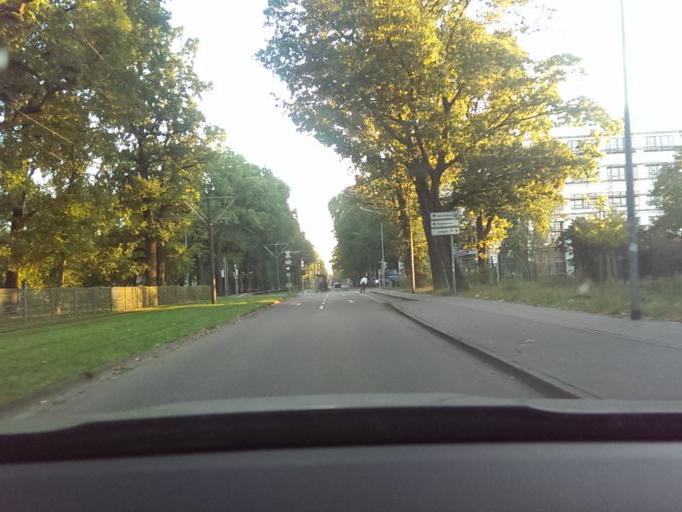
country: DE
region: Baden-Wuerttemberg
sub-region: Karlsruhe Region
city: Karlsruhe
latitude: 49.0281
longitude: 8.3862
